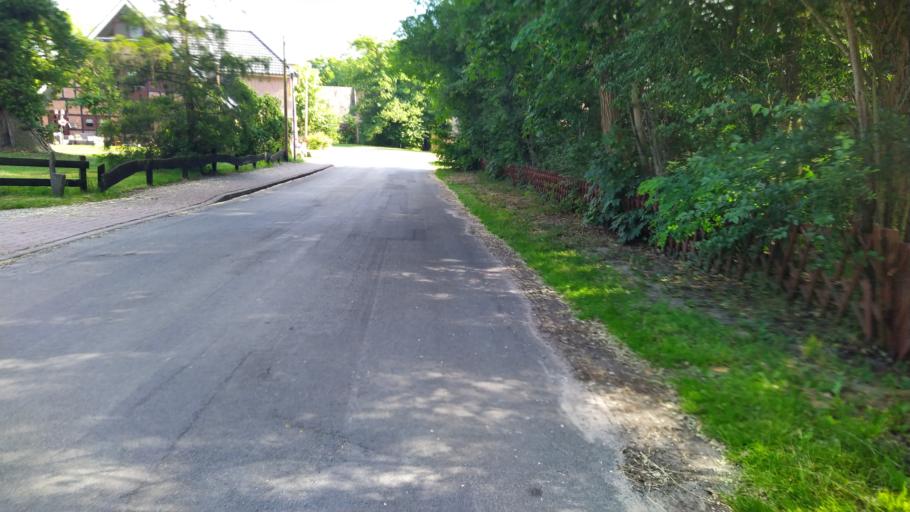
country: DE
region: Lower Saxony
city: Lintig
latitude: 53.6286
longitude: 8.8958
